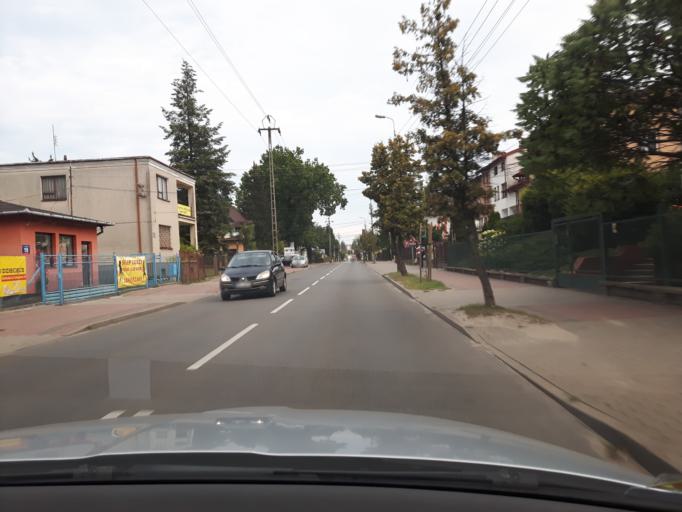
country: PL
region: Masovian Voivodeship
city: Zielonka
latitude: 52.3075
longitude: 21.1560
